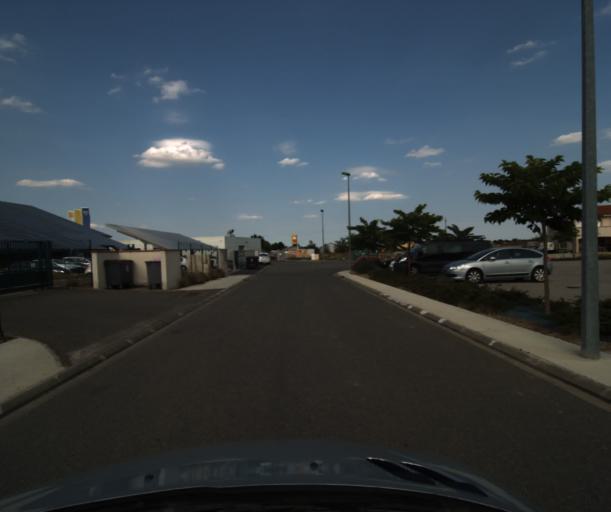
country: FR
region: Midi-Pyrenees
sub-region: Departement de la Haute-Garonne
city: Saint-Lys
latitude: 43.5131
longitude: 1.1994
